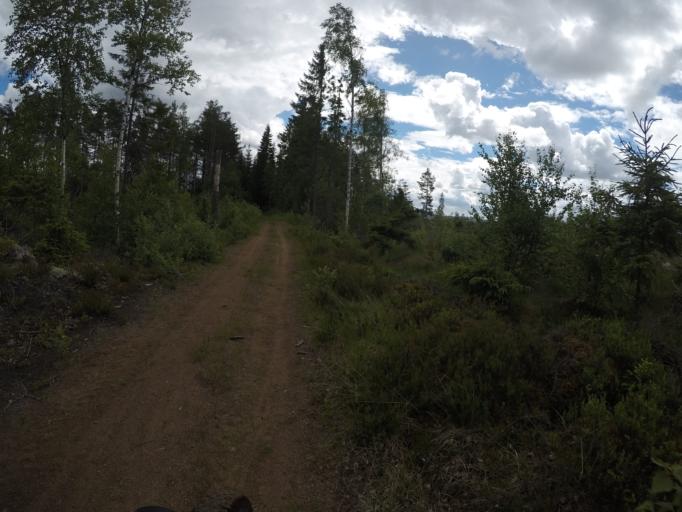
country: SE
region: Vaermland
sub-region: Filipstads Kommun
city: Lesjofors
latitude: 60.1413
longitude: 14.2505
